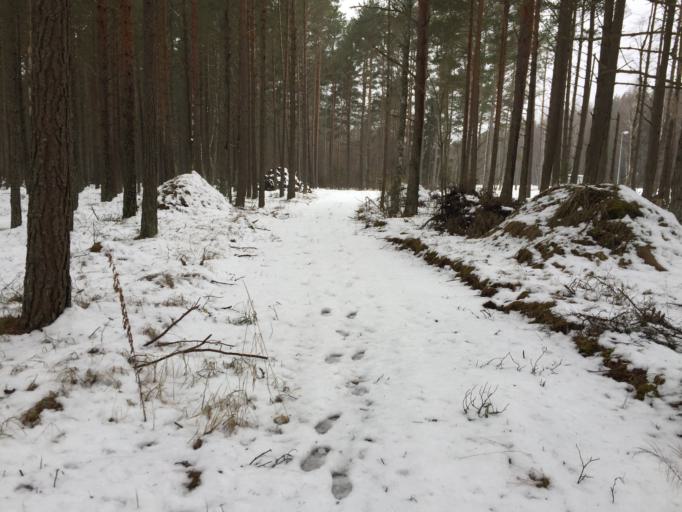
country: EE
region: Saare
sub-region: Kuressaare linn
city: Kuressaare
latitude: 58.2205
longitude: 22.3508
